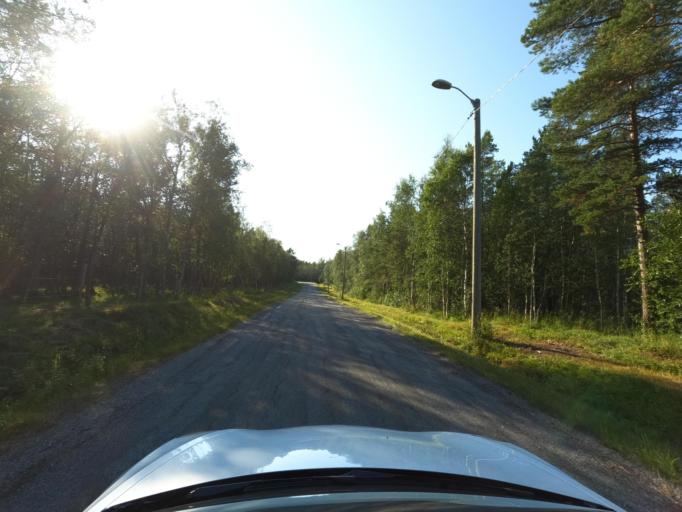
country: NO
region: Nordland
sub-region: Narvik
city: Bjerkvik
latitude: 68.4819
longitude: 17.5326
